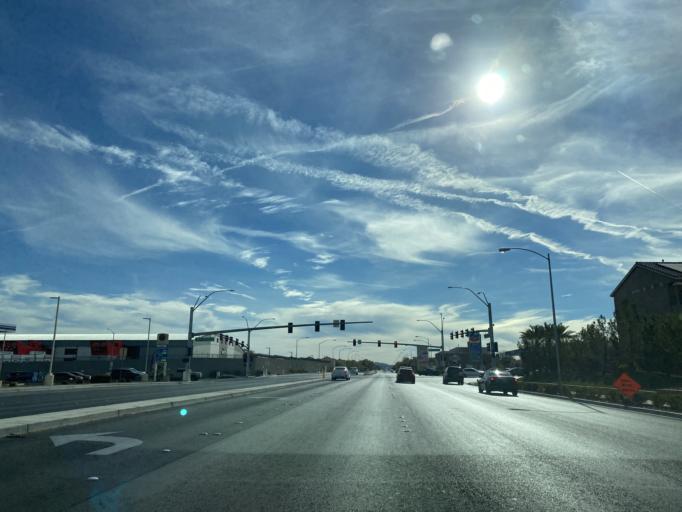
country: US
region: Nevada
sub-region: Clark County
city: Enterprise
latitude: 36.0573
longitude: -115.2250
